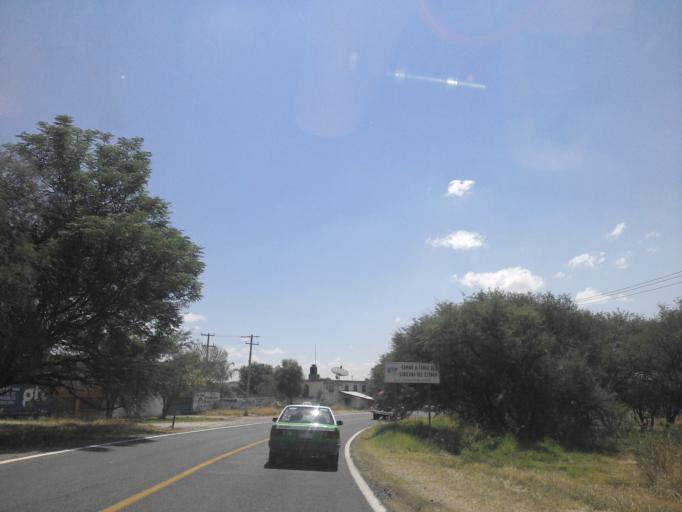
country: MX
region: Guanajuato
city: San Francisco del Rincon
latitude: 21.0249
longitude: -101.8889
